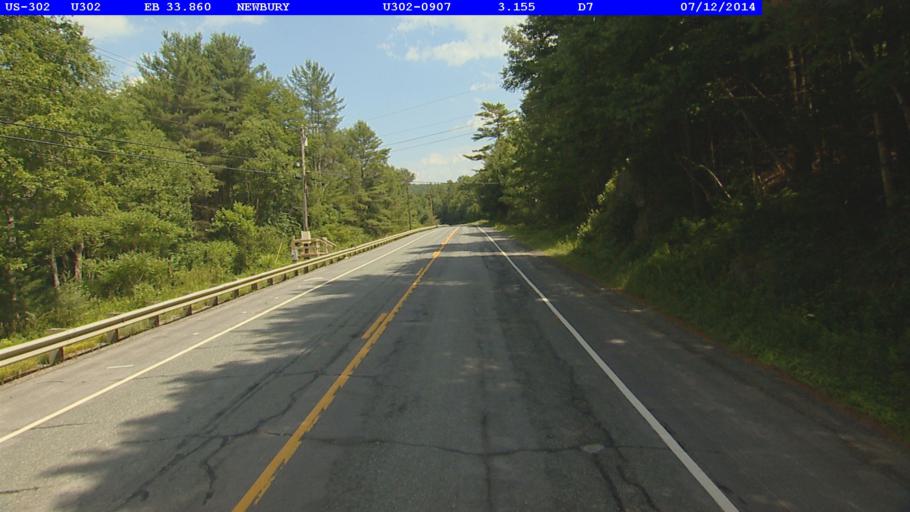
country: US
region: New Hampshire
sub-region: Grafton County
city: Woodsville
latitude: 44.1519
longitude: -72.0725
